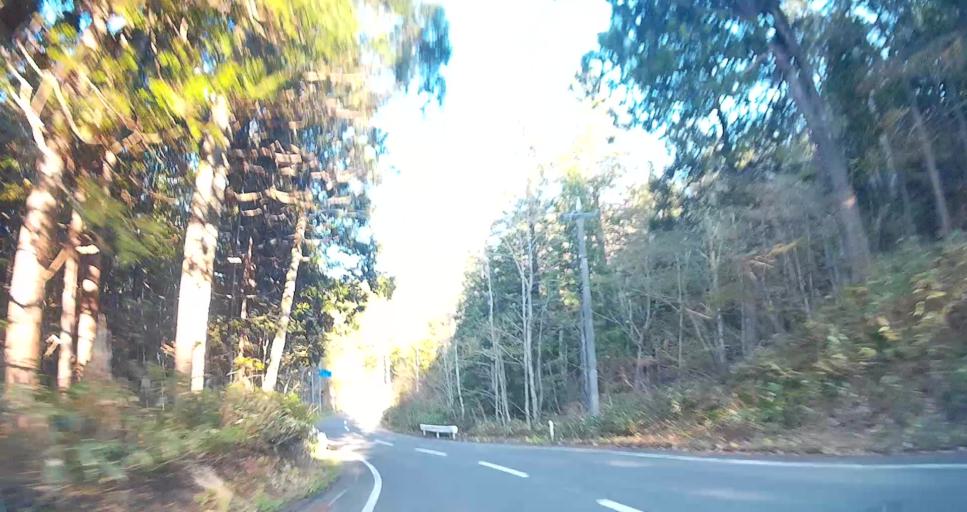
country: JP
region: Aomori
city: Mutsu
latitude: 41.3150
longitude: 141.1241
